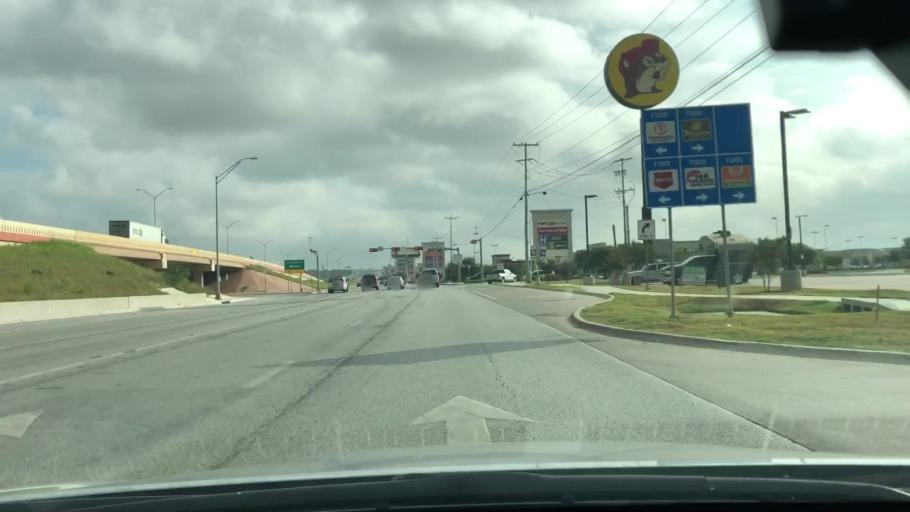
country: US
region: Texas
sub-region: Comal County
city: New Braunfels
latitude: 29.7279
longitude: -98.0788
